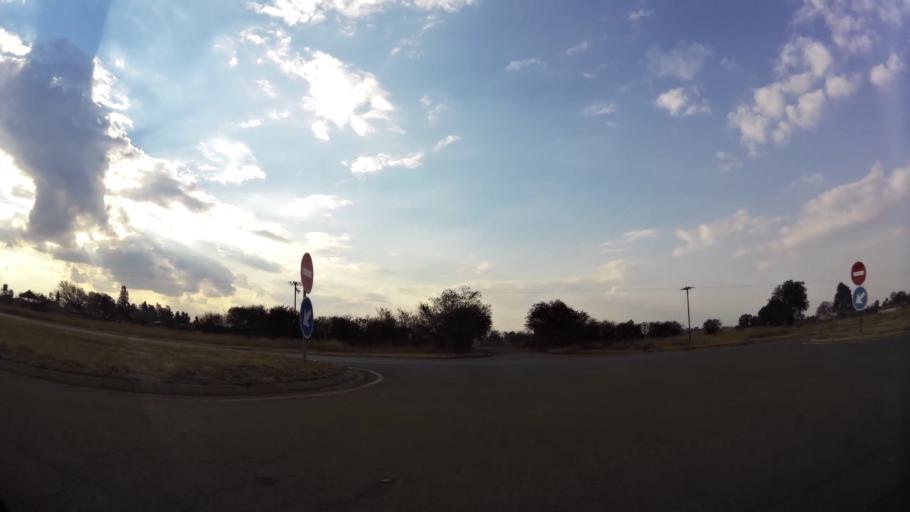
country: ZA
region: Gauteng
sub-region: Sedibeng District Municipality
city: Vanderbijlpark
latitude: -26.6195
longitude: 27.8194
